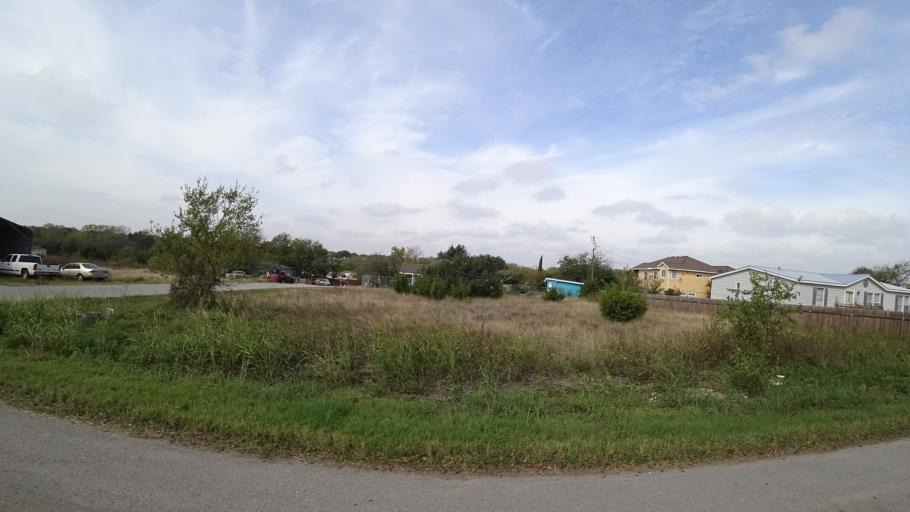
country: US
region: Texas
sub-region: Travis County
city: Wells Branch
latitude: 30.4489
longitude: -97.6714
